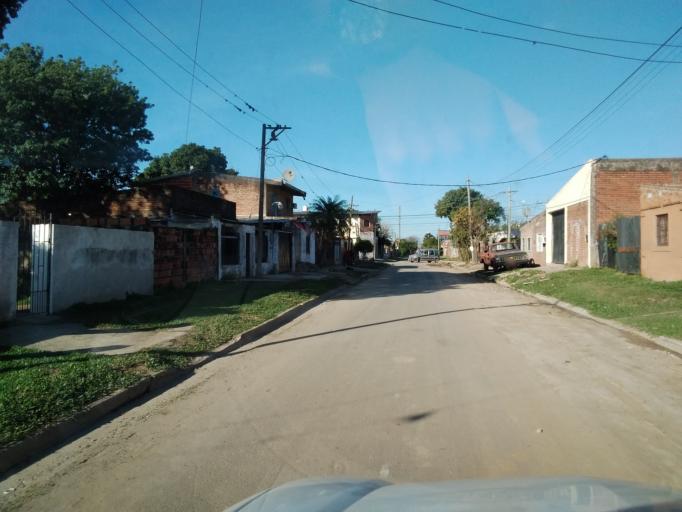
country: AR
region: Corrientes
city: Corrientes
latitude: -27.4944
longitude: -58.8406
